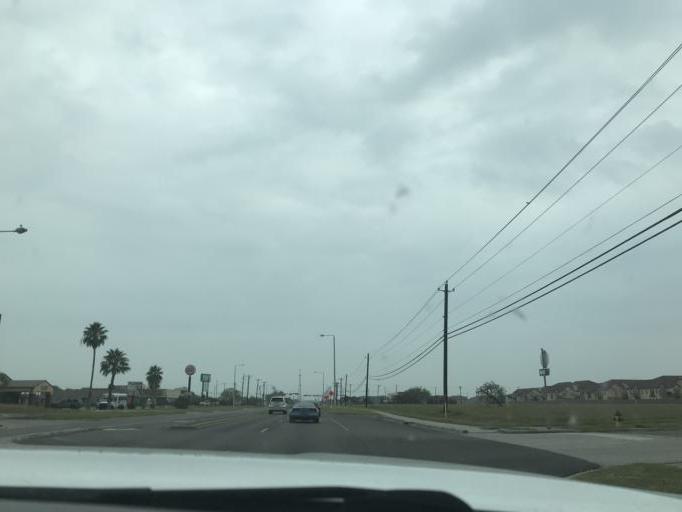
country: US
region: Texas
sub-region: Nueces County
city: Corpus Christi
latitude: 27.6772
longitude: -97.3673
